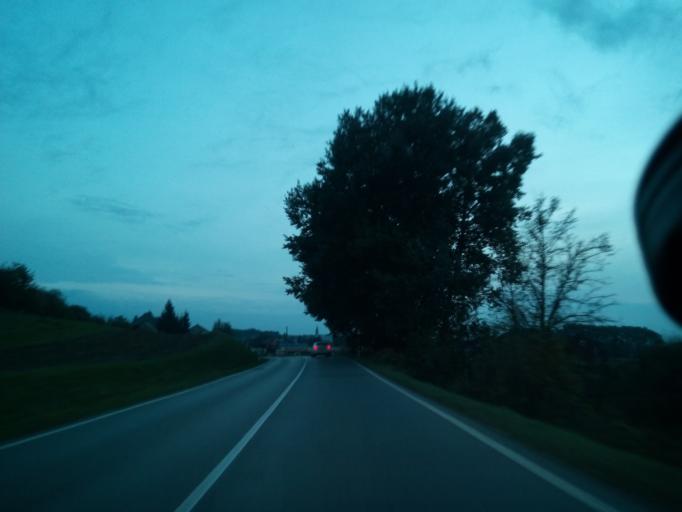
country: SK
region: Presovsky
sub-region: Okres Presov
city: Presov
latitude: 49.0544
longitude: 21.3393
